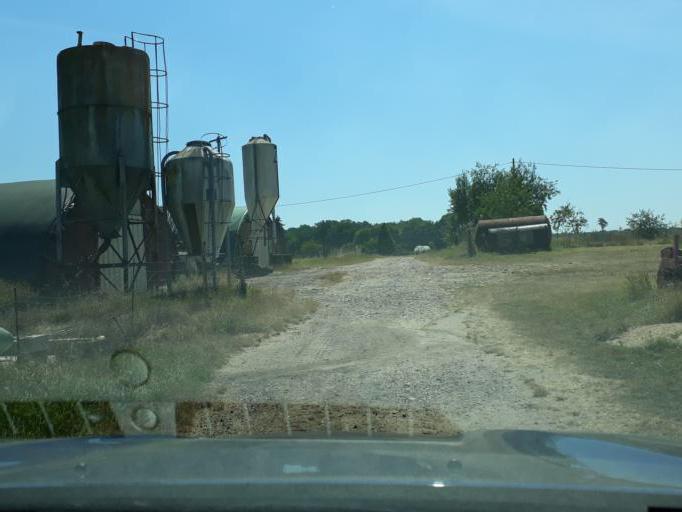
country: FR
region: Centre
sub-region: Departement du Loiret
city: Chevilly
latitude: 47.9922
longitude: 1.9053
